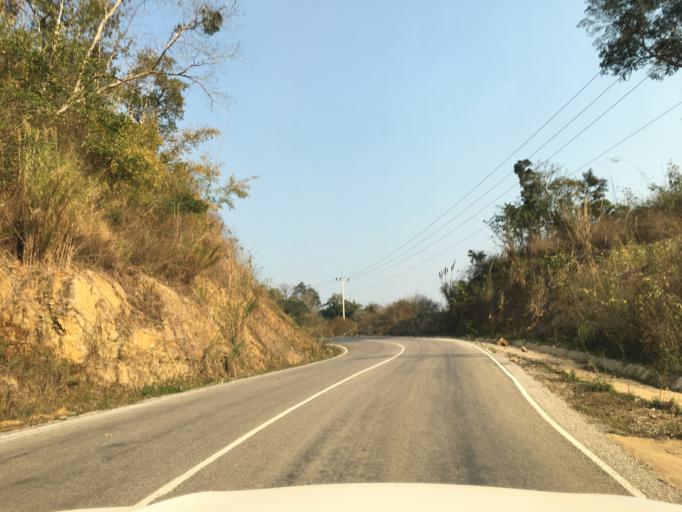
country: LA
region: Houaphan
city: Xam Nua
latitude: 20.5685
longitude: 104.0540
